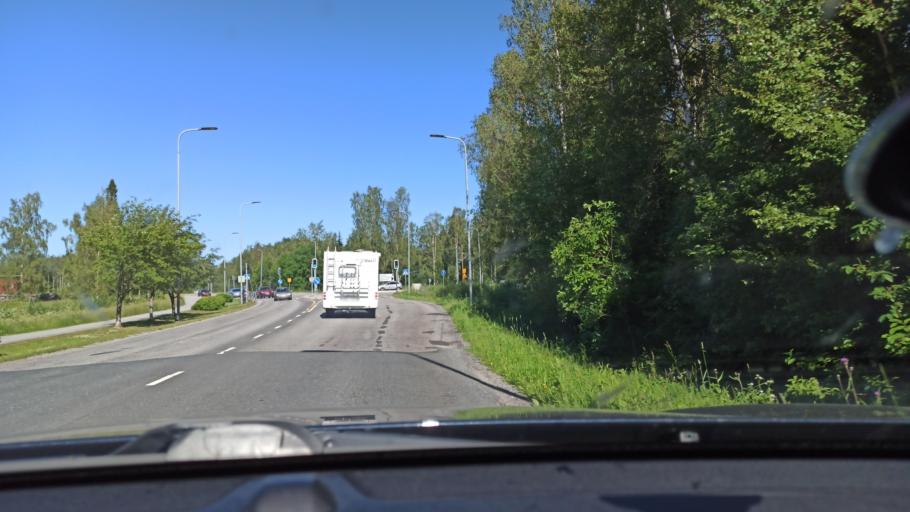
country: FI
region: Ostrobothnia
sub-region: Jakobstadsregionen
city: Jakobstad
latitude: 63.6687
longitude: 22.7117
